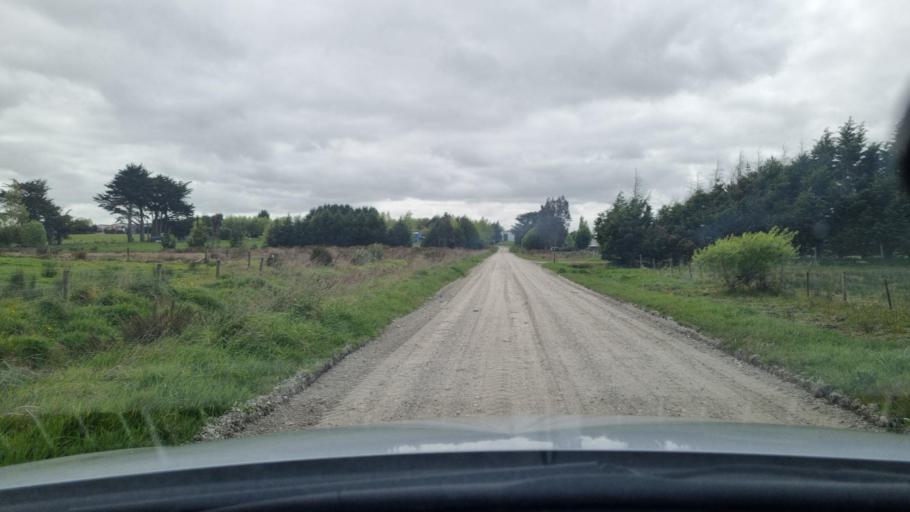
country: NZ
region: Southland
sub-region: Invercargill City
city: Invercargill
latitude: -46.4352
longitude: 168.3897
